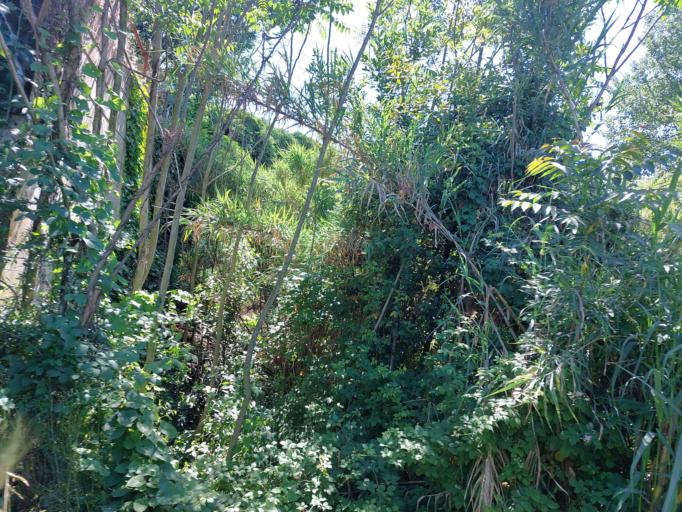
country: IT
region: Latium
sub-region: Citta metropolitana di Roma Capitale
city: Rome
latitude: 41.8539
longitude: 12.5509
